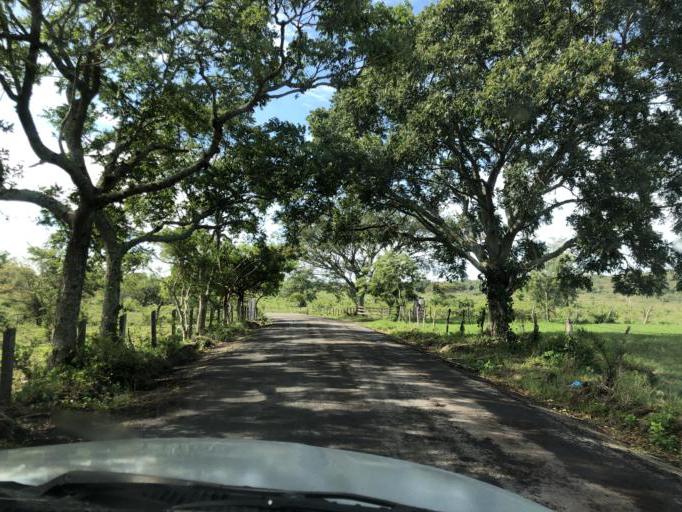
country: MX
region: Veracruz
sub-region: Alto Lucero de Gutierrez Barrios
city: Palma Sola
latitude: 19.8063
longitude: -96.5440
